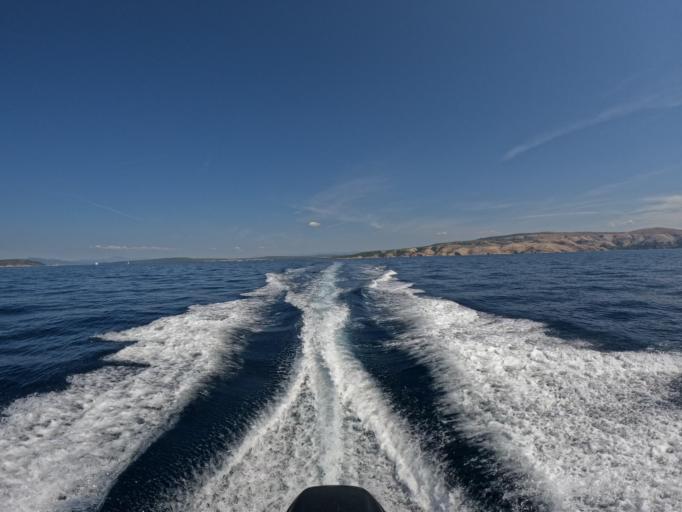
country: HR
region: Primorsko-Goranska
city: Punat
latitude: 44.9341
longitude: 14.6163
